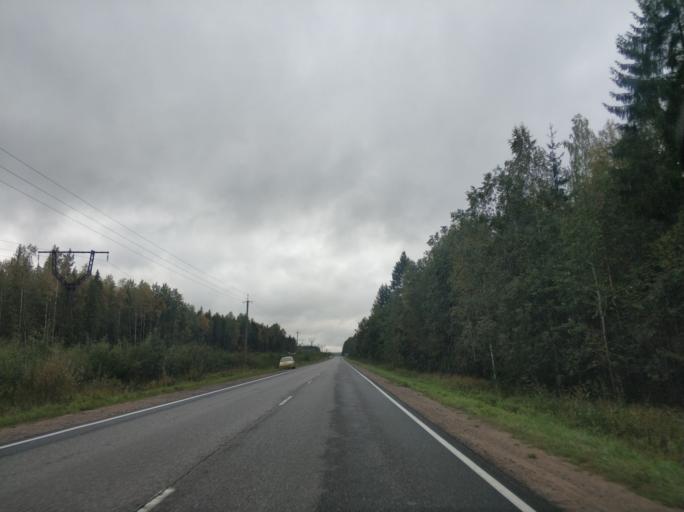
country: RU
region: Leningrad
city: Borisova Griva
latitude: 60.1034
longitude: 30.9574
